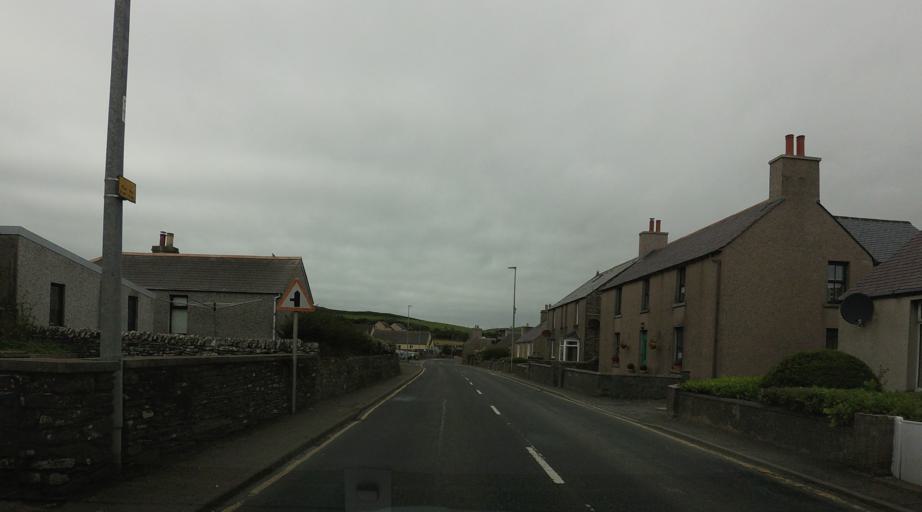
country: GB
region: Scotland
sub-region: Orkney Islands
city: Orkney
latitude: 59.0038
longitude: -3.1092
